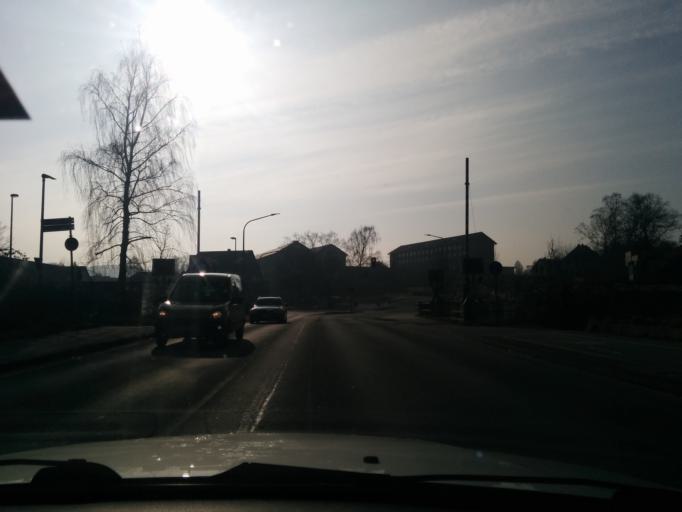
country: DE
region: North Rhine-Westphalia
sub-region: Regierungsbezirk Detmold
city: Lemgo
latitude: 52.0210
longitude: 8.9117
